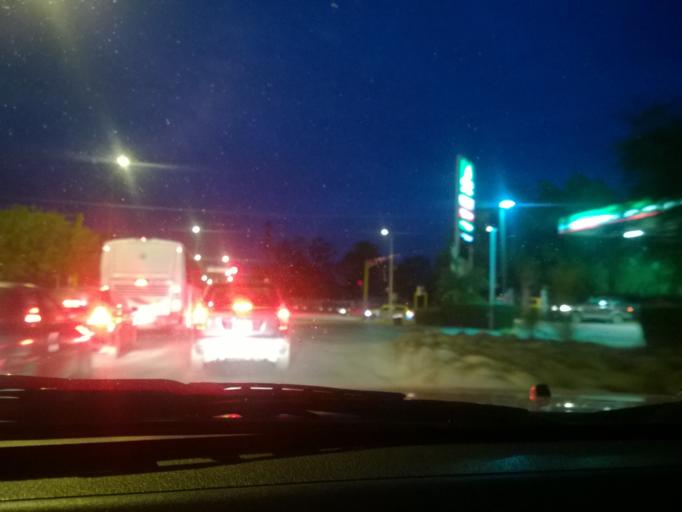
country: MX
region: Guanajuato
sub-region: Leon
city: Fraccionamiento Paraiso Real
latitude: 21.1132
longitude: -101.6051
